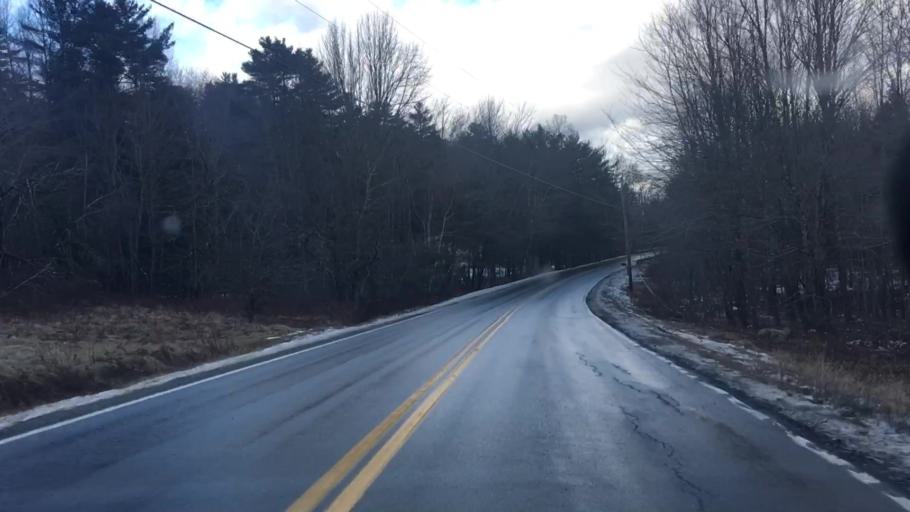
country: US
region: Maine
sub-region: Hancock County
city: Dedham
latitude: 44.6419
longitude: -68.6967
